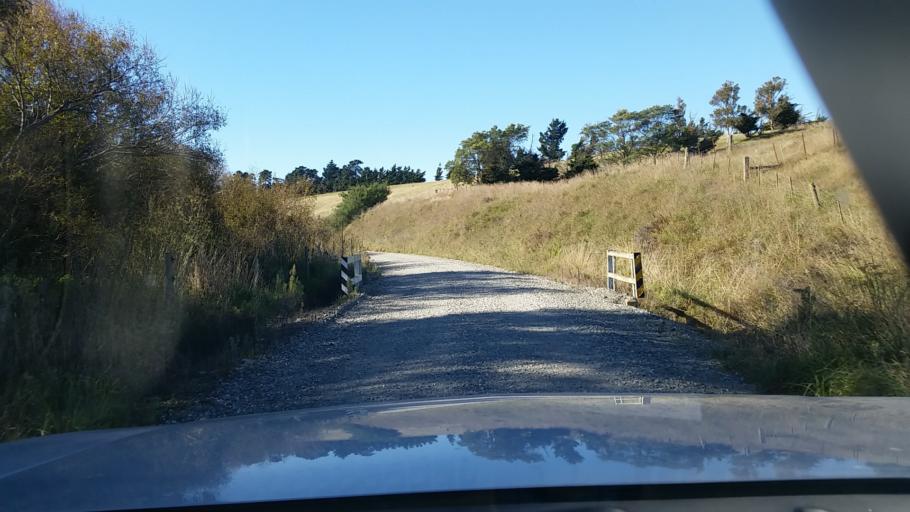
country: NZ
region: Marlborough
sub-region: Marlborough District
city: Blenheim
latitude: -41.6782
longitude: 174.1416
